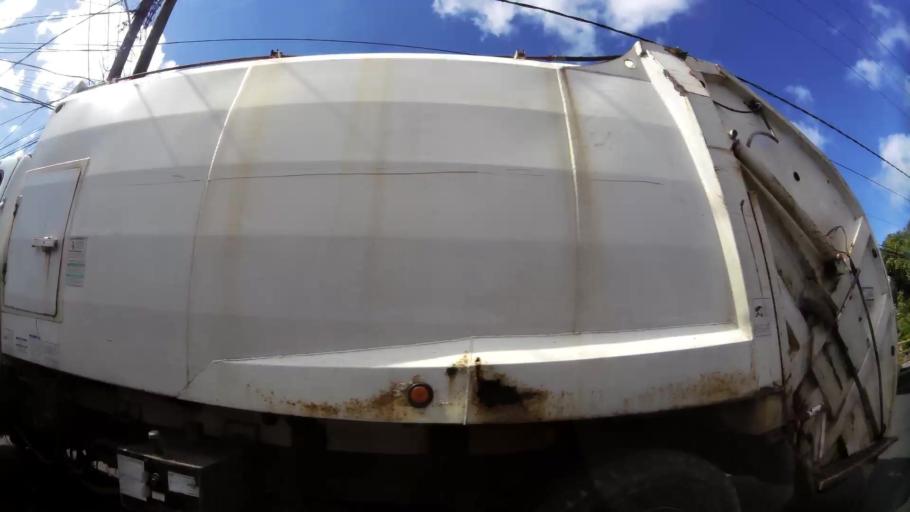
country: DM
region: Saint John
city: Portsmouth
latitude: 15.5777
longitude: -61.4574
